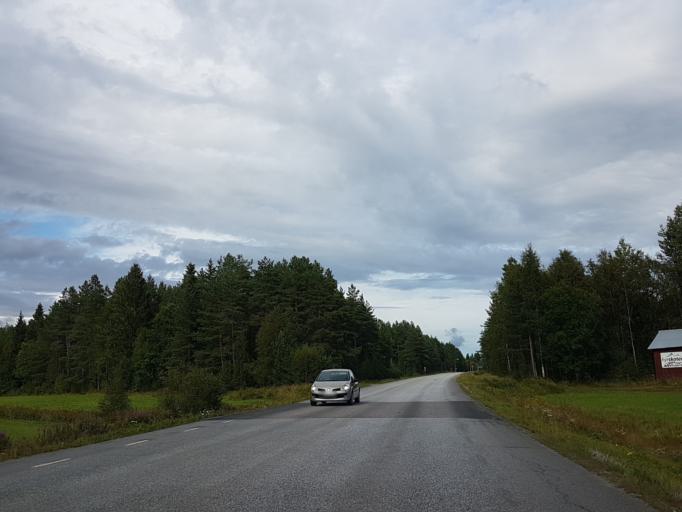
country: SE
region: Vaesterbotten
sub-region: Umea Kommun
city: Taftea
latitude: 63.8319
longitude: 20.4655
